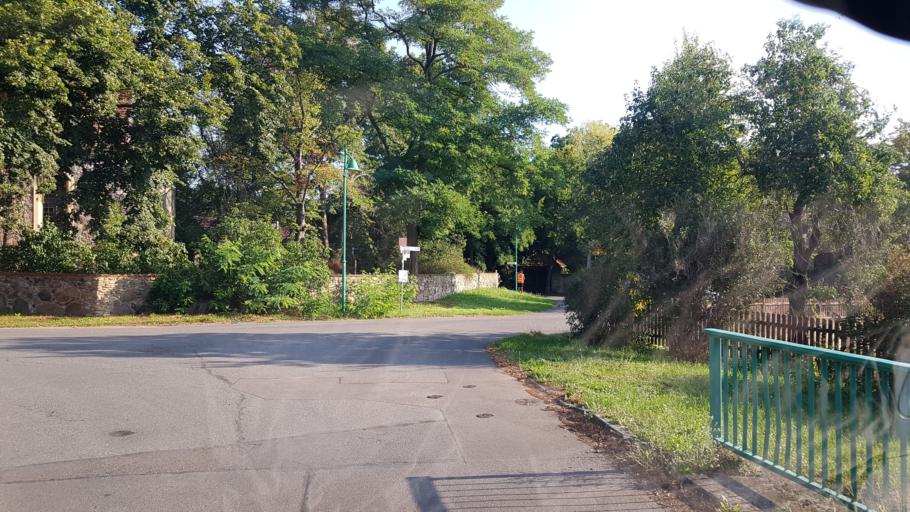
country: DE
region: Brandenburg
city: Luckau
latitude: 51.8030
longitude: 13.6497
